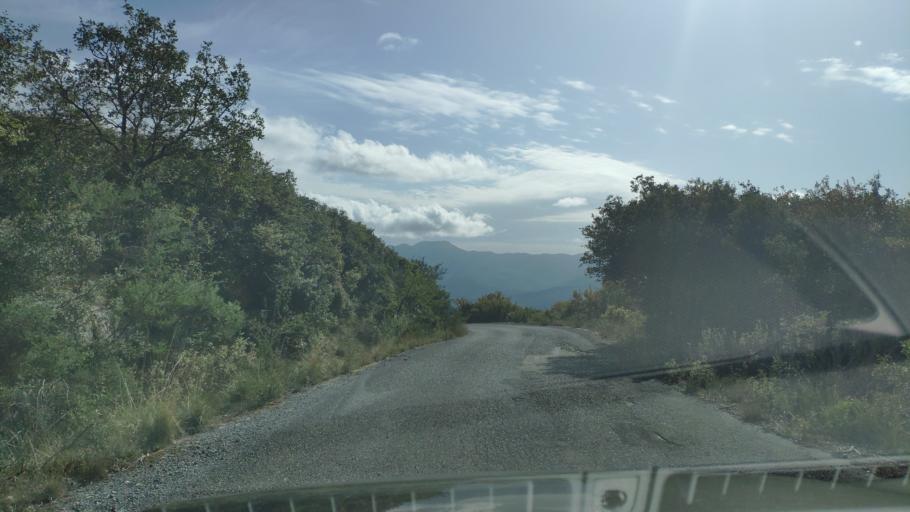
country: GR
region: Peloponnese
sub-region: Nomos Arkadias
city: Dimitsana
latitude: 37.5722
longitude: 22.0033
